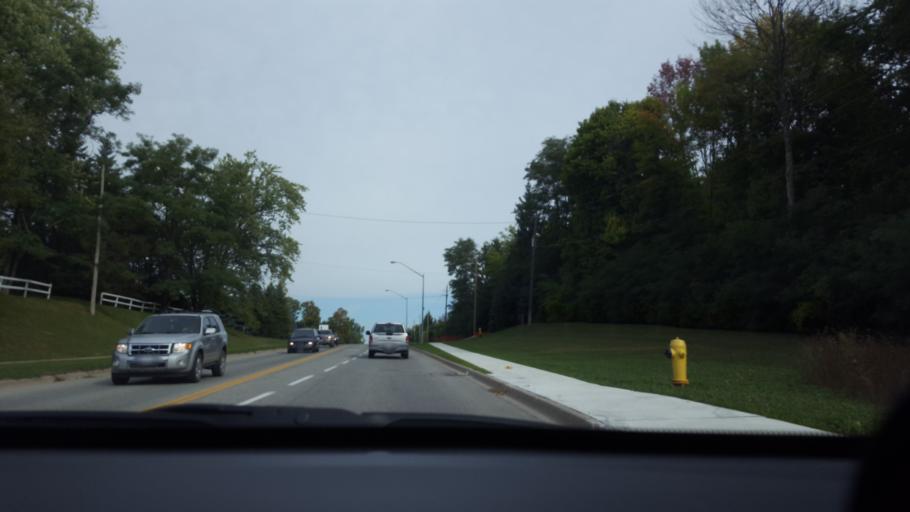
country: CA
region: Ontario
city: Vaughan
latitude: 43.9362
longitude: -79.5302
